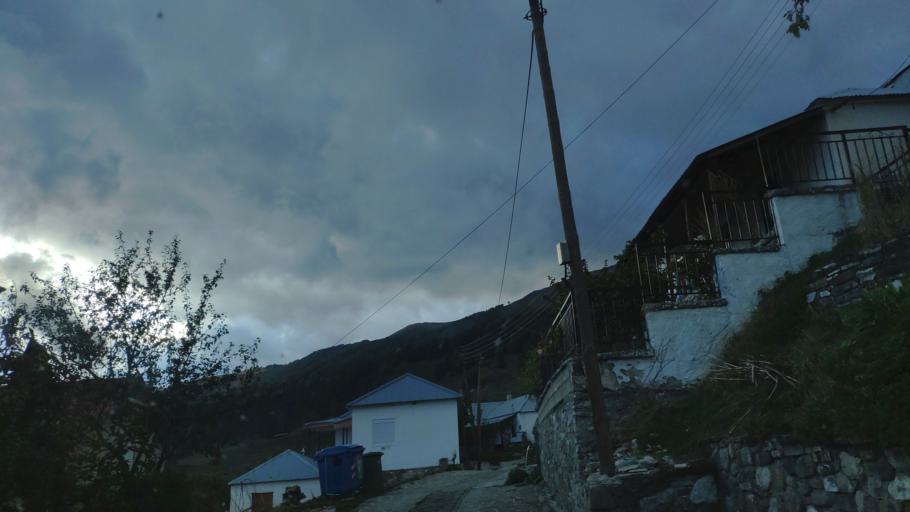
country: AL
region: Korce
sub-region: Rrethi i Kolonjes
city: Erseke
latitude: 40.3107
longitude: 20.8545
